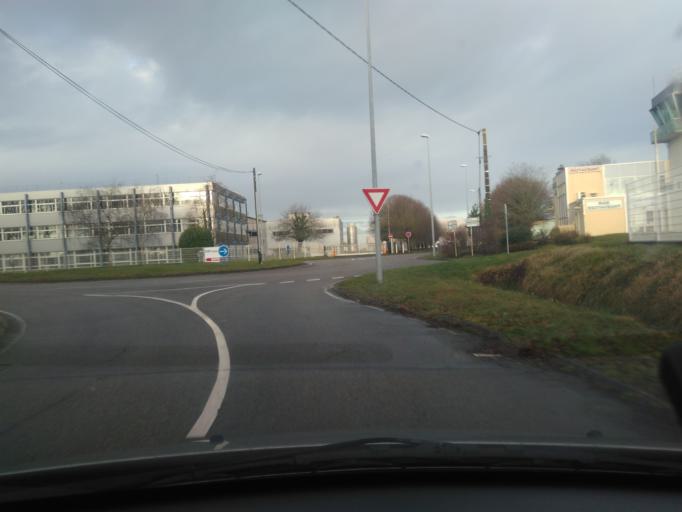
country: FR
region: Pays de la Loire
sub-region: Departement de la Vendee
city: Dompierre-sur-Yon
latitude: 46.6990
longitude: -1.3768
